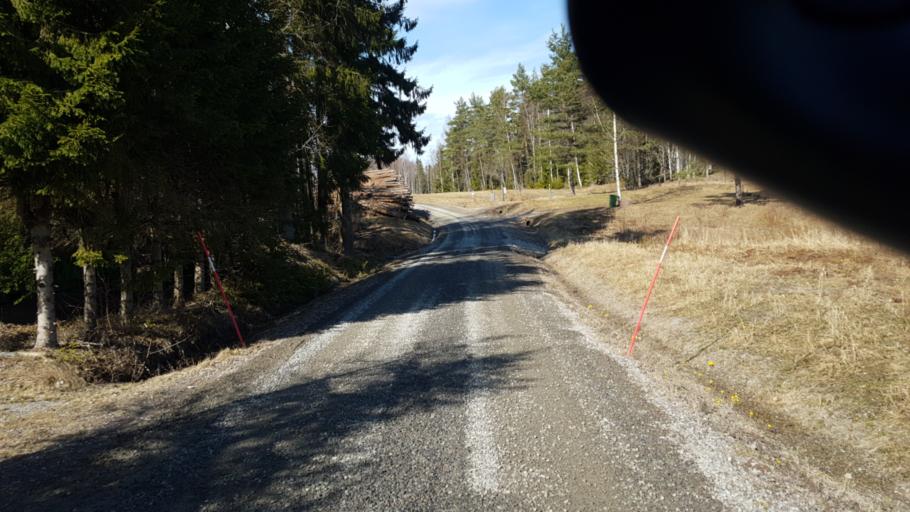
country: SE
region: Vaermland
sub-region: Arvika Kommun
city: Arvika
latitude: 59.5708
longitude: 12.8348
